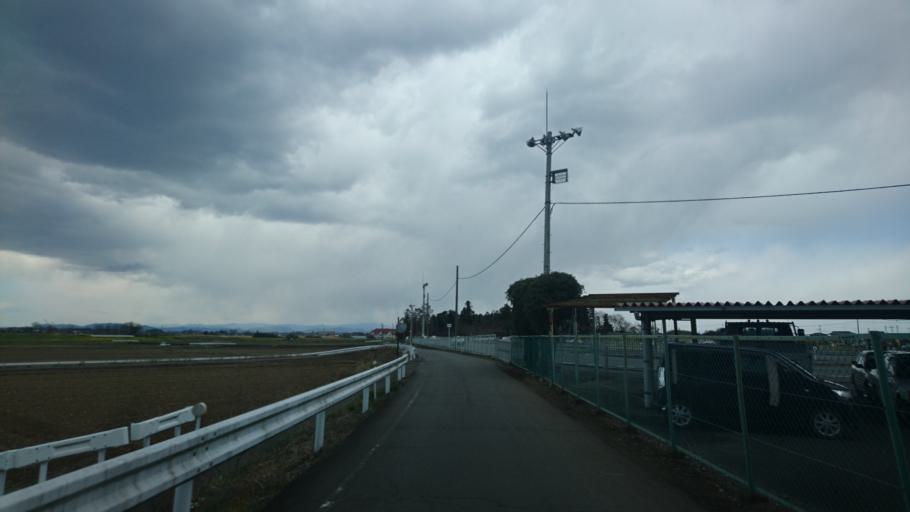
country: JP
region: Ibaraki
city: Yuki
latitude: 36.2688
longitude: 139.9117
